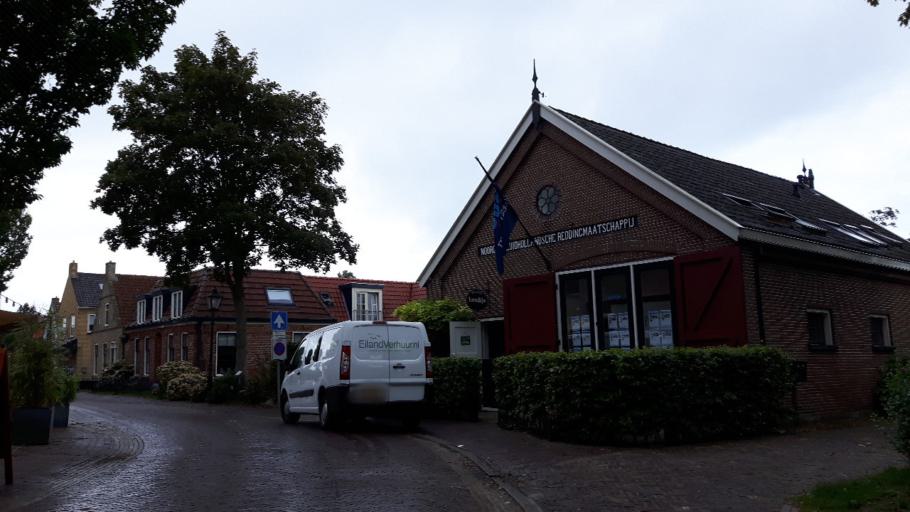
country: NL
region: Friesland
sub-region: Gemeente Ameland
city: Nes
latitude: 53.4465
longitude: 5.7711
